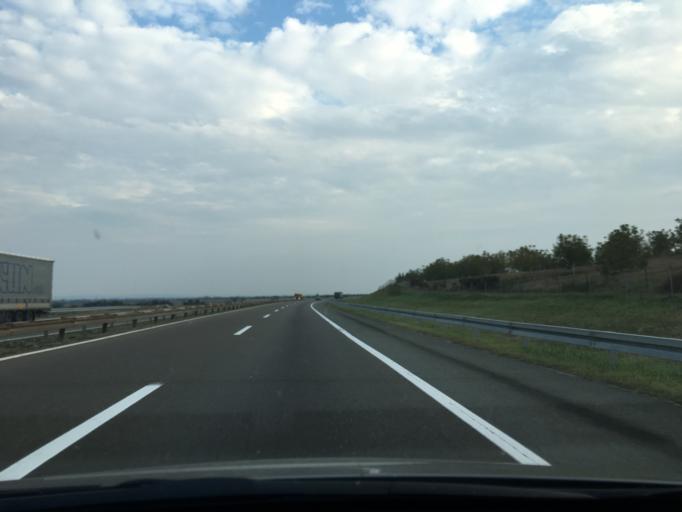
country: RS
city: Lugavcina
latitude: 44.4568
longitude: 21.0418
